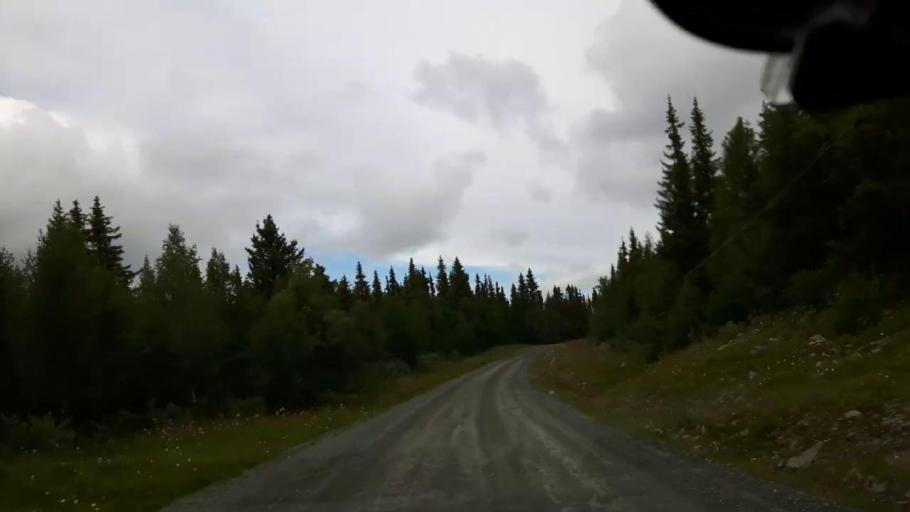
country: SE
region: Jaemtland
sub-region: Krokoms Kommun
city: Valla
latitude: 63.7701
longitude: 13.8305
